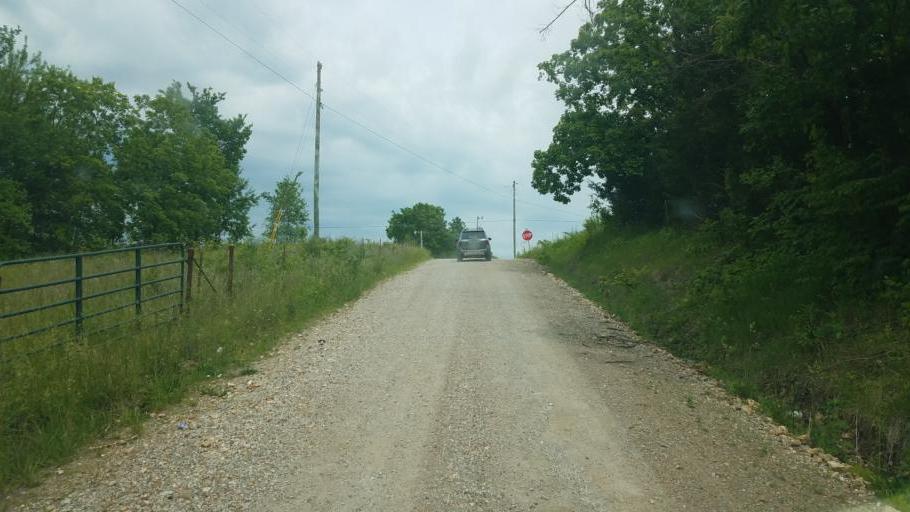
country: US
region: Missouri
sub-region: Moniteau County
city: California
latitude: 38.6460
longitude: -92.5715
